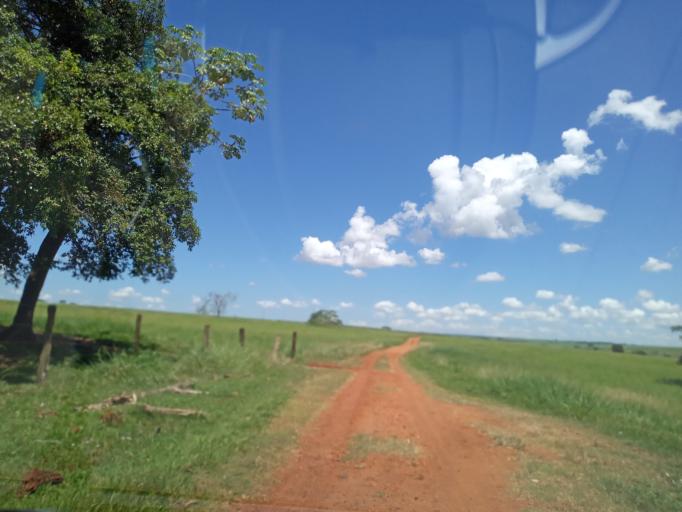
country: BR
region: Goias
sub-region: Itumbiara
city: Itumbiara
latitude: -18.3989
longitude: -49.1275
